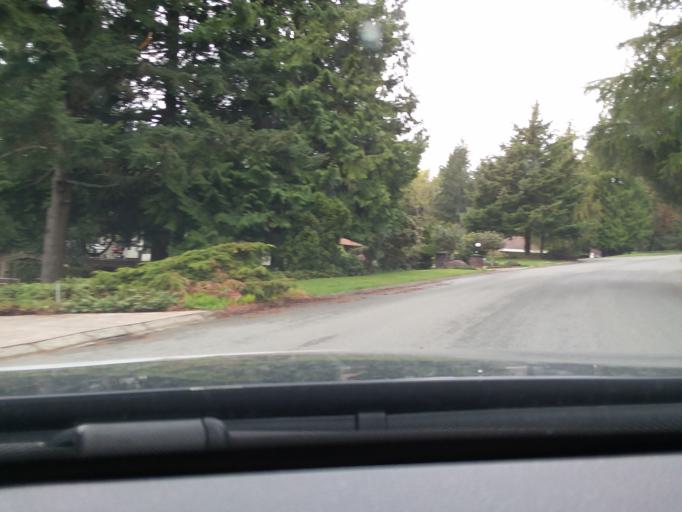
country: CA
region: British Columbia
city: North Saanich
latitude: 48.6153
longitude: -123.4265
